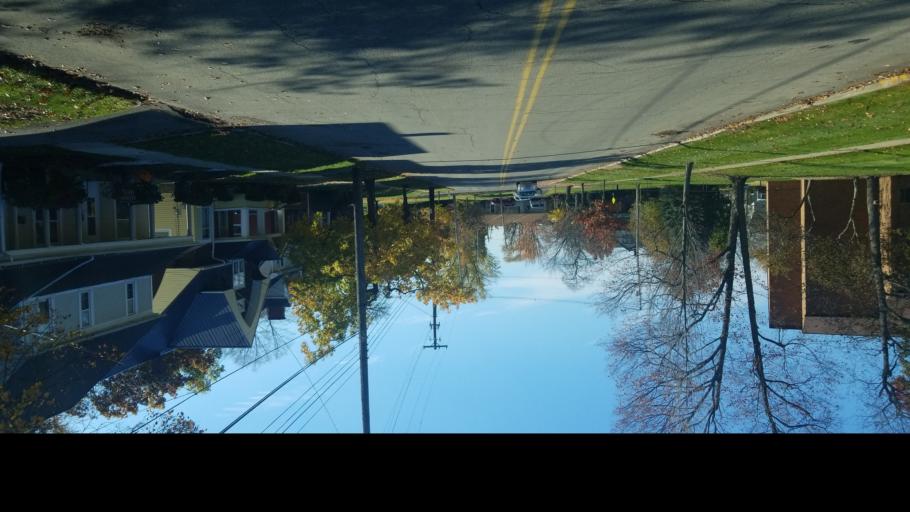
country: US
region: Ohio
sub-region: Ashland County
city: Ashland
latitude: 40.8624
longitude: -82.3135
